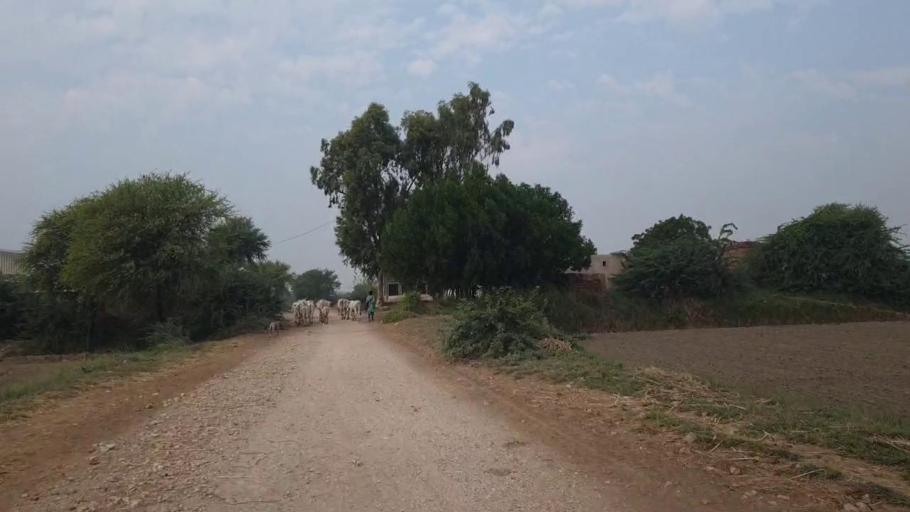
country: PK
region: Sindh
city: Tando Bago
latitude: 24.7898
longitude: 68.8826
